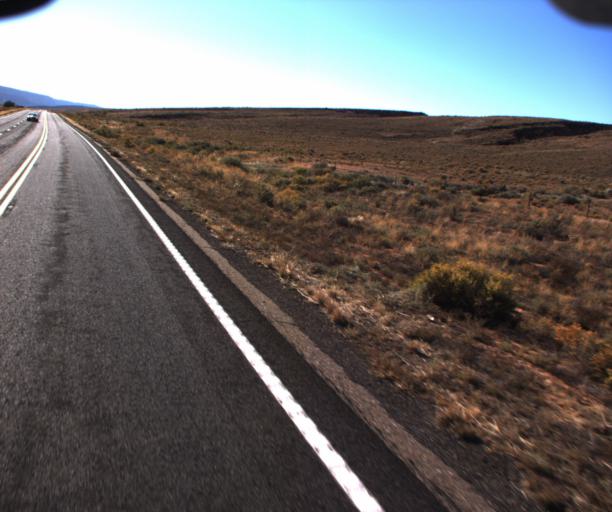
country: US
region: Arizona
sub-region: Coconino County
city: LeChee
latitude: 36.5599
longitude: -111.6345
